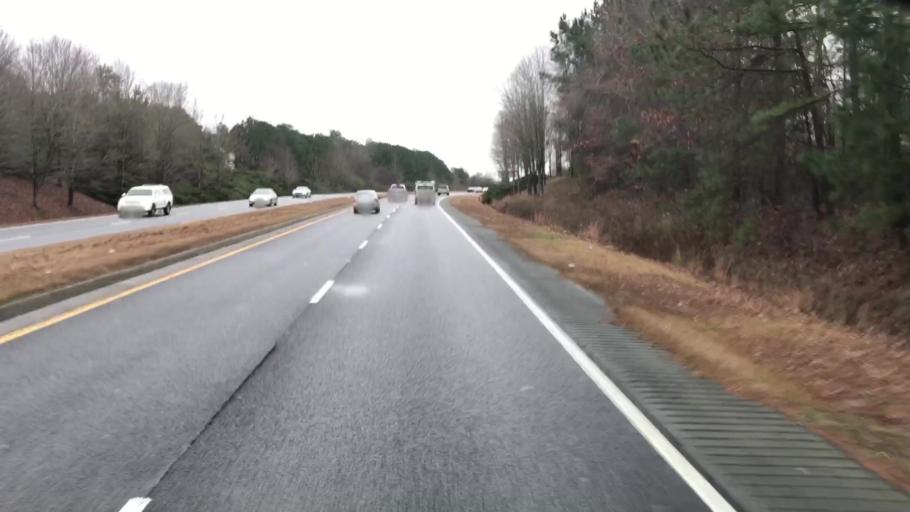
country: US
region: Georgia
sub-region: Gwinnett County
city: Snellville
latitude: 33.8832
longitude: -84.0311
